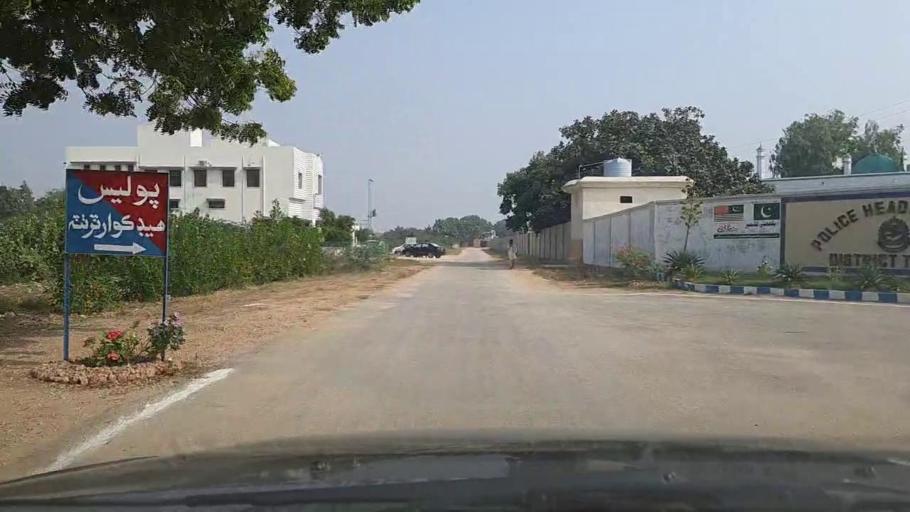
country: PK
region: Sindh
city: Thatta
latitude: 24.7420
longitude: 67.8941
